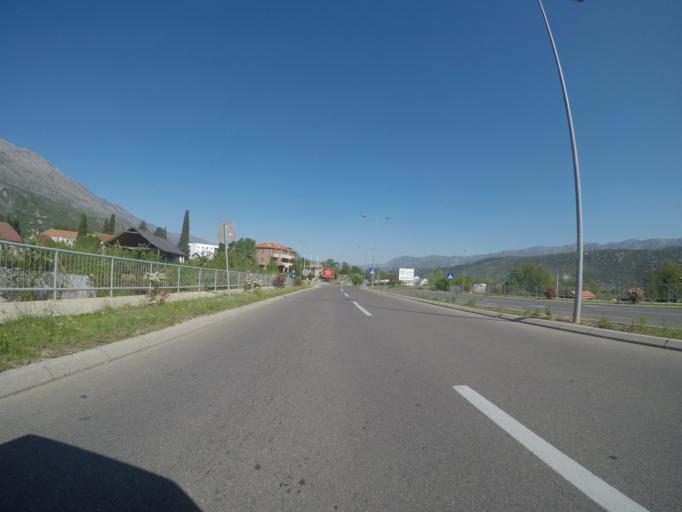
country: ME
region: Danilovgrad
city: Danilovgrad
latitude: 42.5531
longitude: 19.0896
